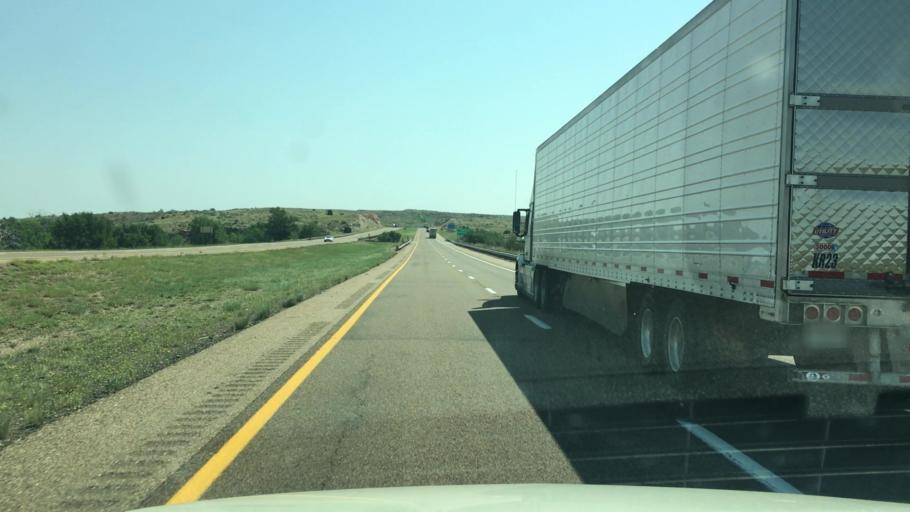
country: US
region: New Mexico
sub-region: Quay County
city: Tucumcari
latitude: 35.1477
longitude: -103.7934
